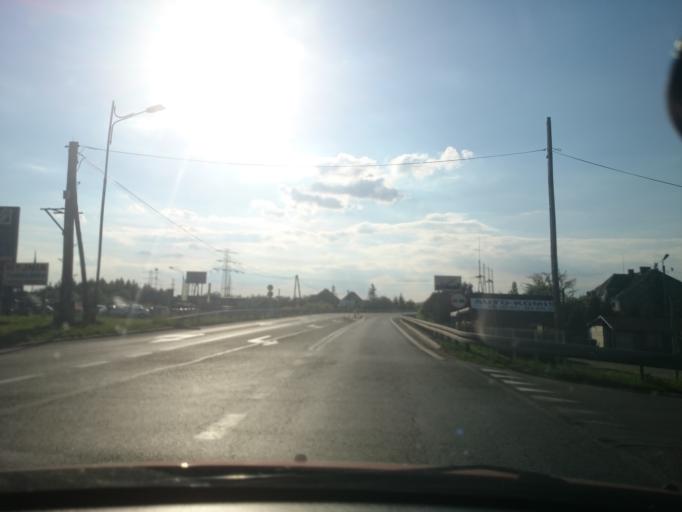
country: PL
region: Opole Voivodeship
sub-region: Powiat strzelecki
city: Strzelce Opolskie
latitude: 50.5203
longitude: 18.2822
